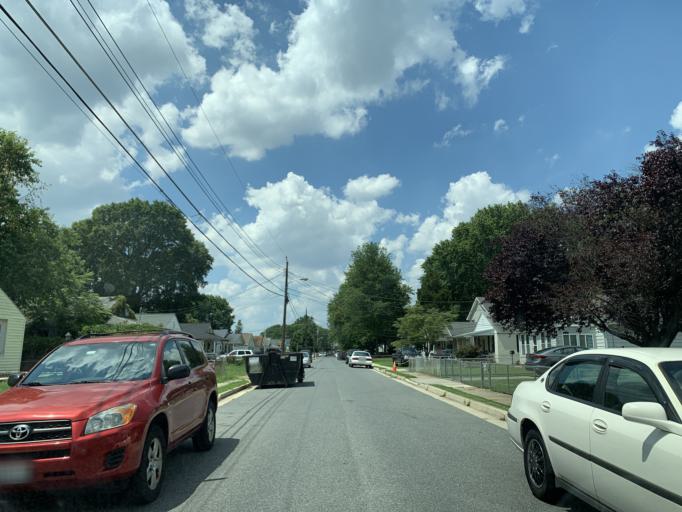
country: US
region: Maryland
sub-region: Baltimore County
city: Essex
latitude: 39.3068
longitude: -76.4602
